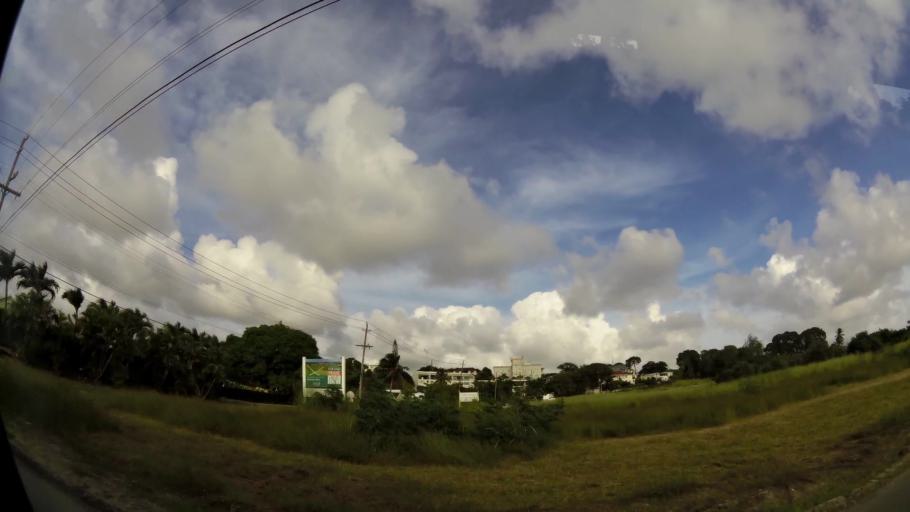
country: BB
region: Christ Church
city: Oistins
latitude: 13.0936
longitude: -59.5702
